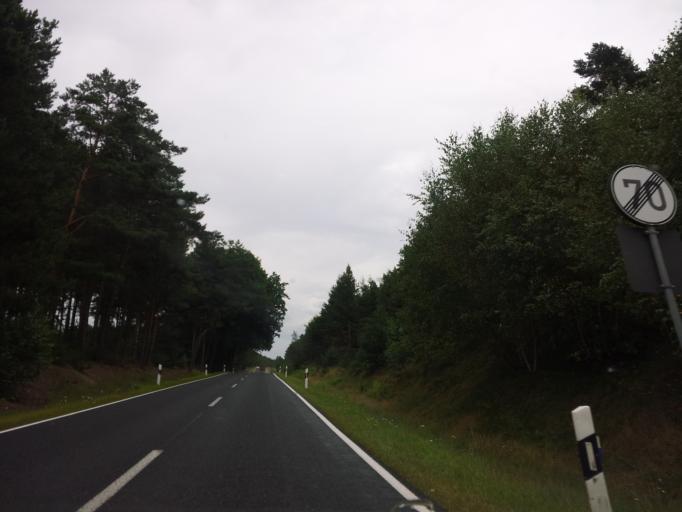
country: DE
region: Brandenburg
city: Gorzke
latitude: 52.1716
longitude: 12.4130
